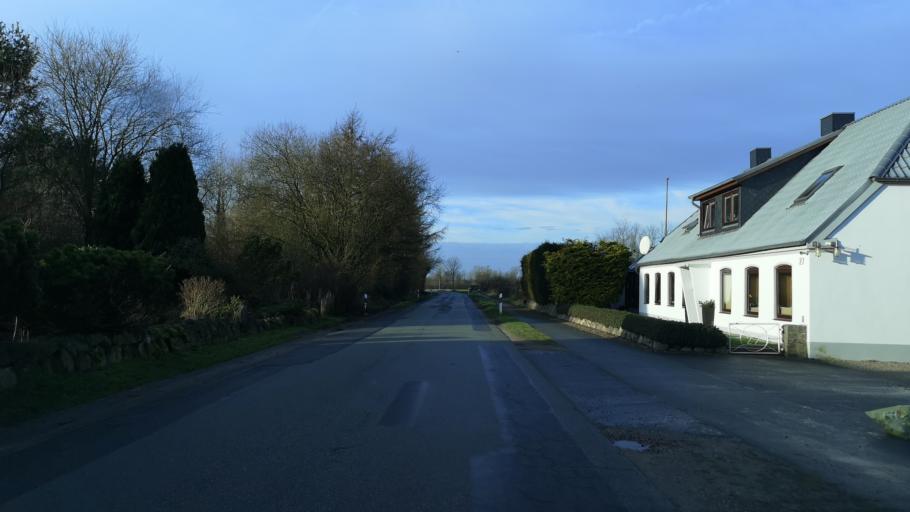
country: DE
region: Schleswig-Holstein
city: Havetoft
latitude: 54.6603
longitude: 9.5442
